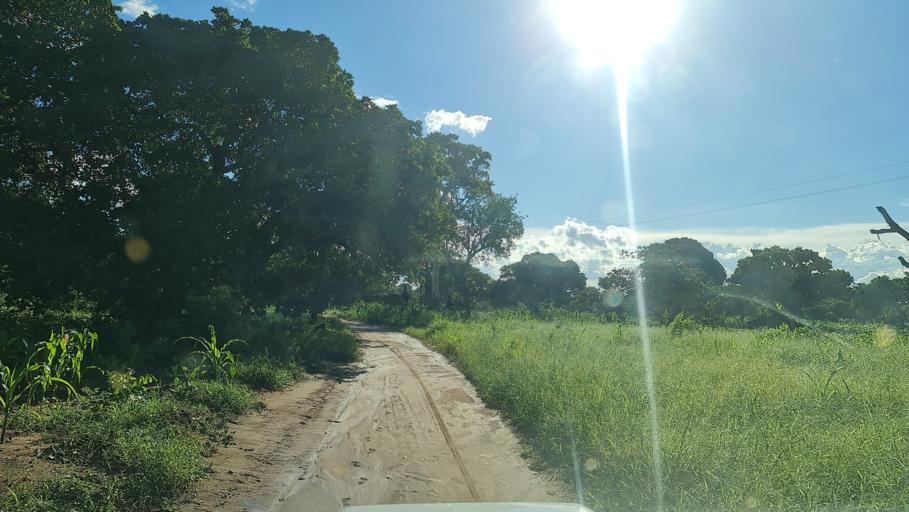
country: MZ
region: Nampula
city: Ilha de Mocambique
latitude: -14.9308
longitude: 40.2182
